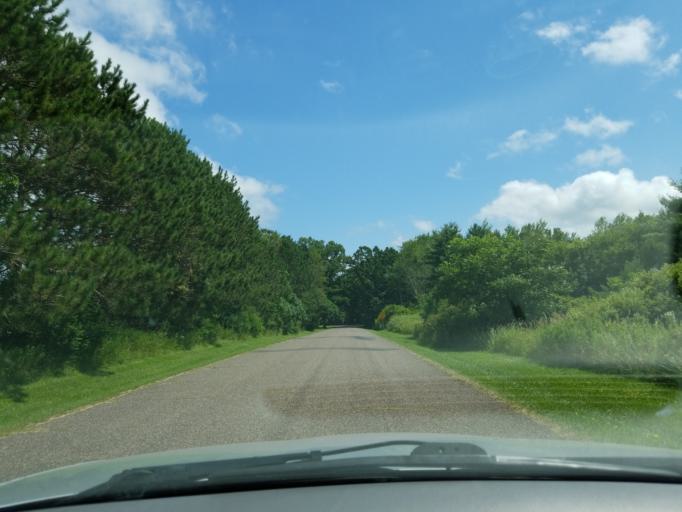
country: US
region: Wisconsin
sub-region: Saint Croix County
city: Glenwood City
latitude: 45.0066
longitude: -92.1730
